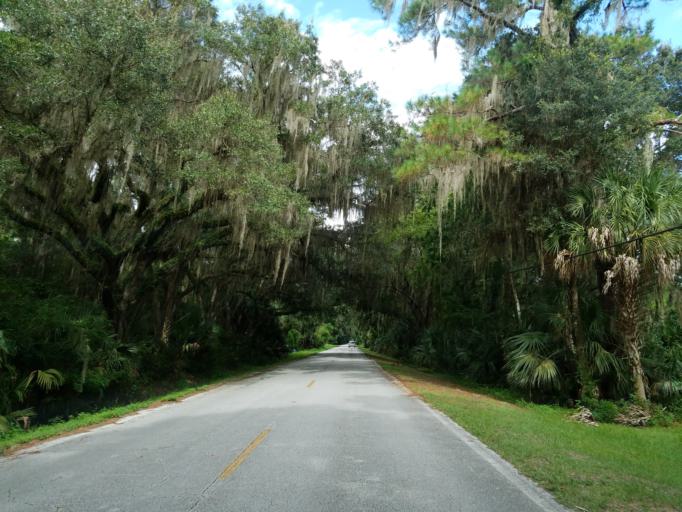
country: US
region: Florida
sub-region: Alachua County
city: Gainesville
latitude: 29.5026
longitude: -82.2722
